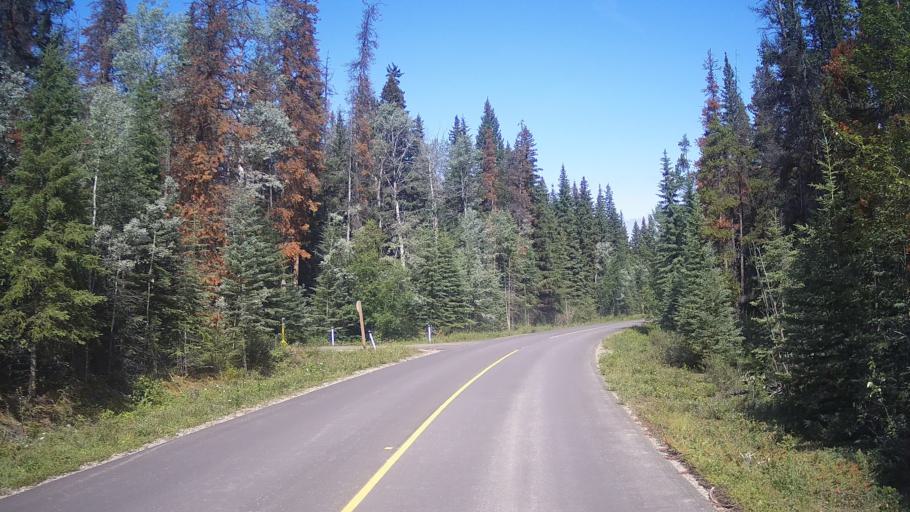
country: CA
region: Alberta
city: Jasper Park Lodge
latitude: 52.7448
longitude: -117.9708
